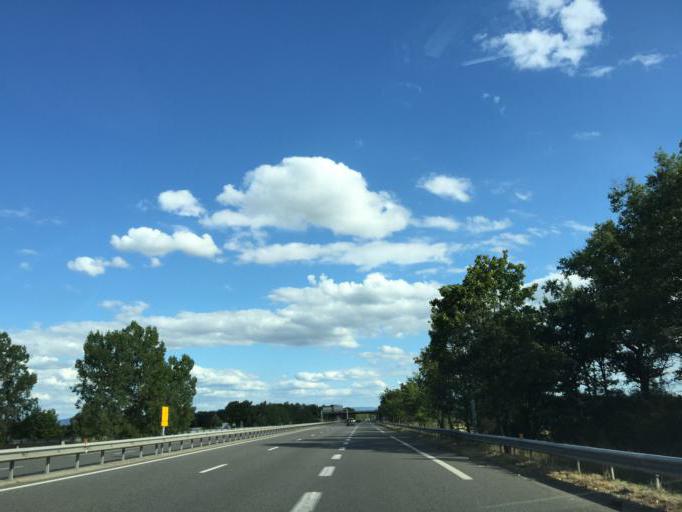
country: FR
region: Rhone-Alpes
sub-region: Departement de la Loire
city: Montrond-les-Bains
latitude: 45.6380
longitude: 4.1910
